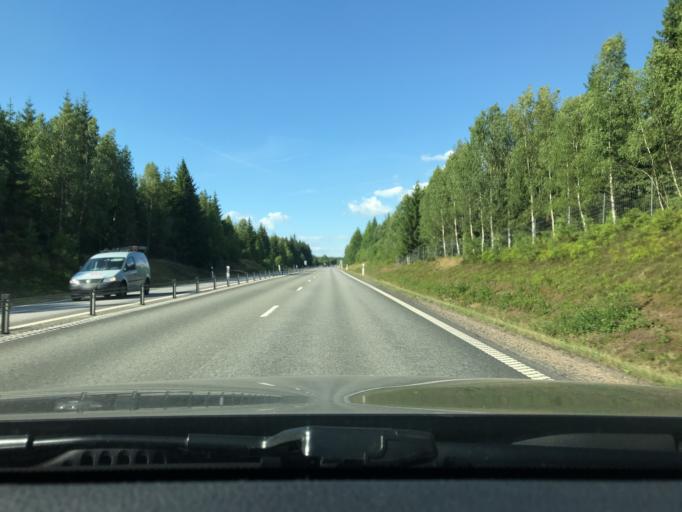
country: SE
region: Skane
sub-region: Osby Kommun
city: Osby
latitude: 56.4246
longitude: 14.0557
